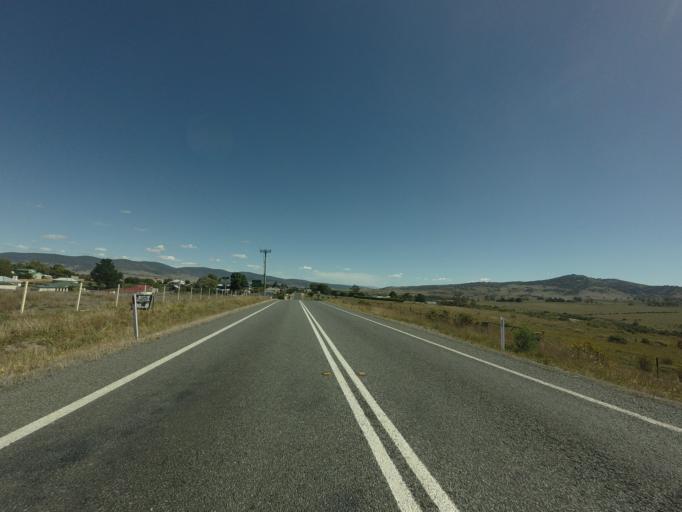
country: AU
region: Tasmania
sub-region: Northern Midlands
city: Evandale
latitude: -41.7791
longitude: 147.7266
